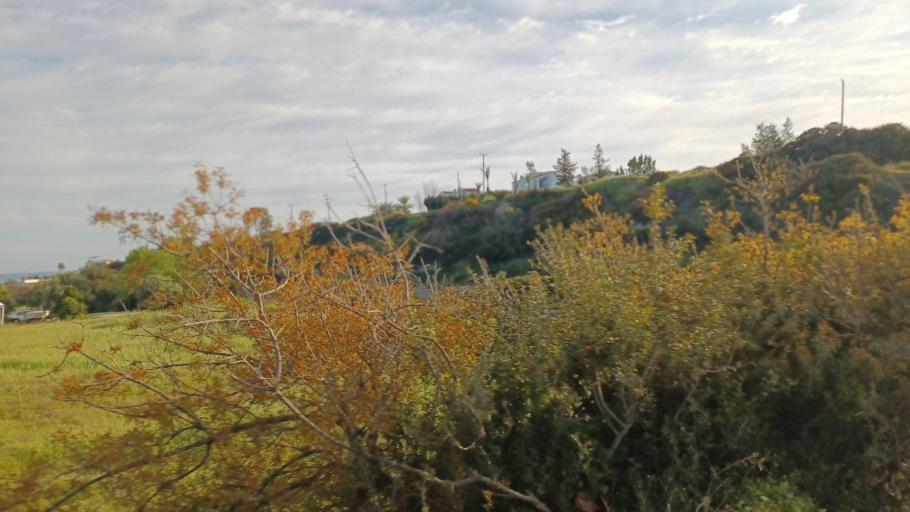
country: CY
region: Pafos
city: Polis
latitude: 35.0333
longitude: 32.3968
